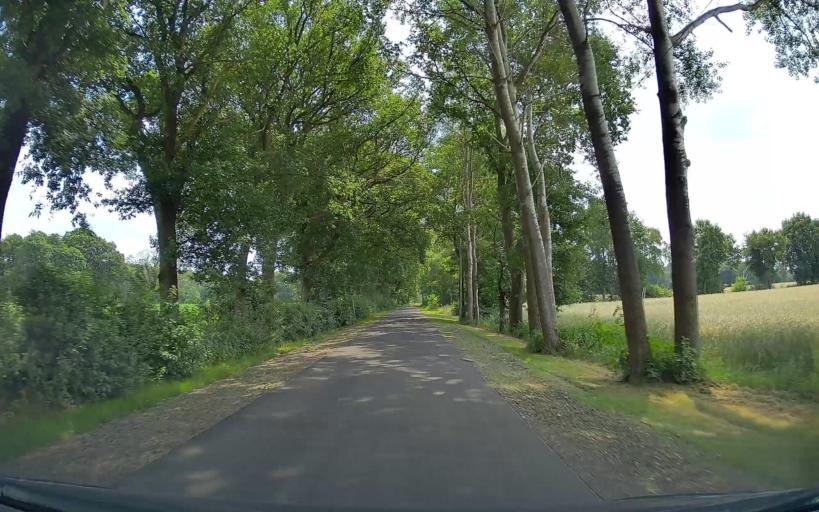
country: DE
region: Lower Saxony
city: Friesoythe
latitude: 52.9888
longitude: 7.8821
